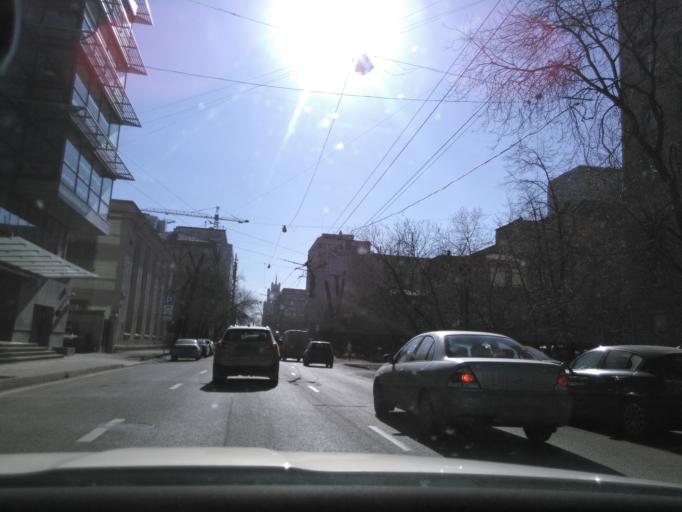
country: RU
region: Moskovskaya
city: Dorogomilovo
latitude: 55.7733
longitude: 37.5866
